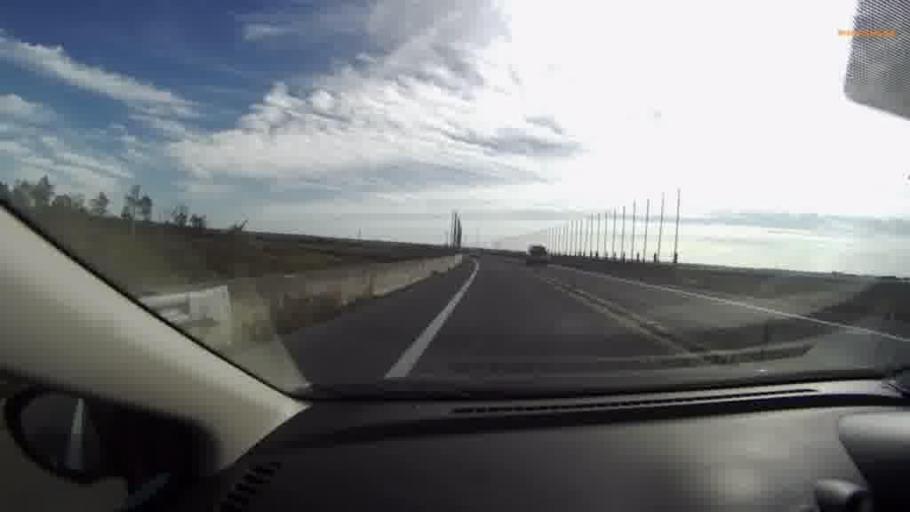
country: JP
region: Hokkaido
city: Kushiro
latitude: 43.0352
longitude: 144.3653
